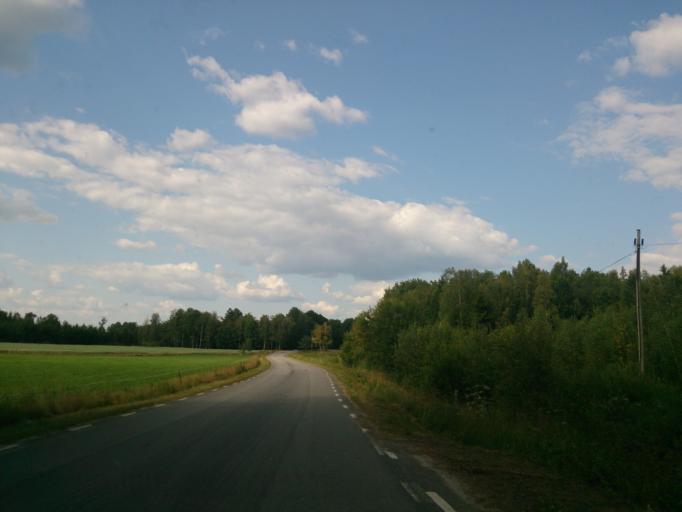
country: SE
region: Joenkoeping
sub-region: Varnamo Kommun
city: Forsheda
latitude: 57.0699
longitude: 13.8005
